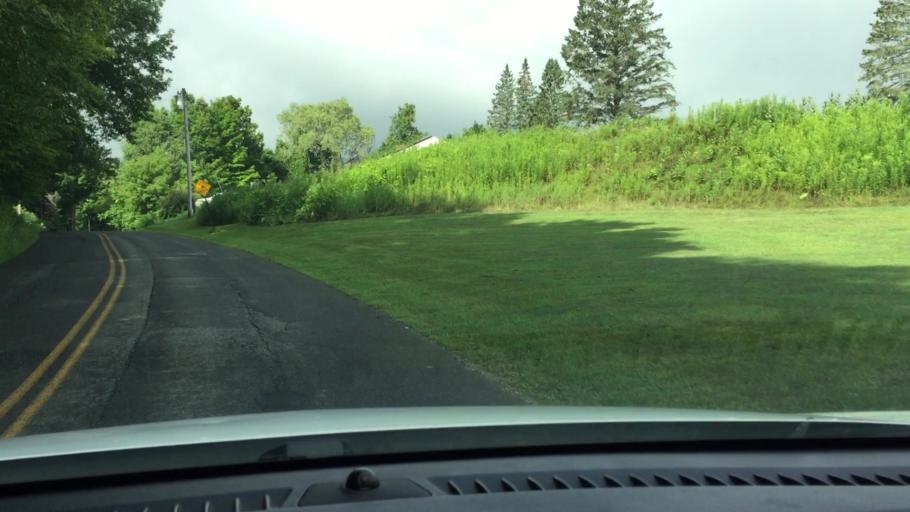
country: US
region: Massachusetts
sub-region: Berkshire County
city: Hinsdale
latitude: 42.4413
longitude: -73.1211
